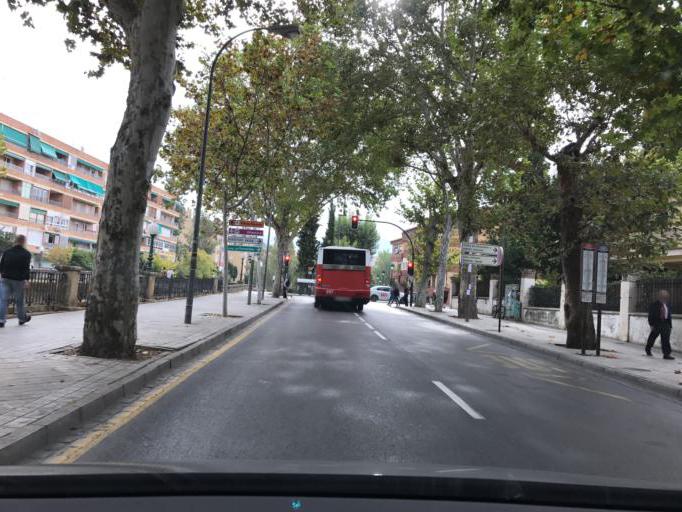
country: ES
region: Andalusia
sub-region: Provincia de Granada
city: Granada
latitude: 37.1675
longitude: -3.5902
